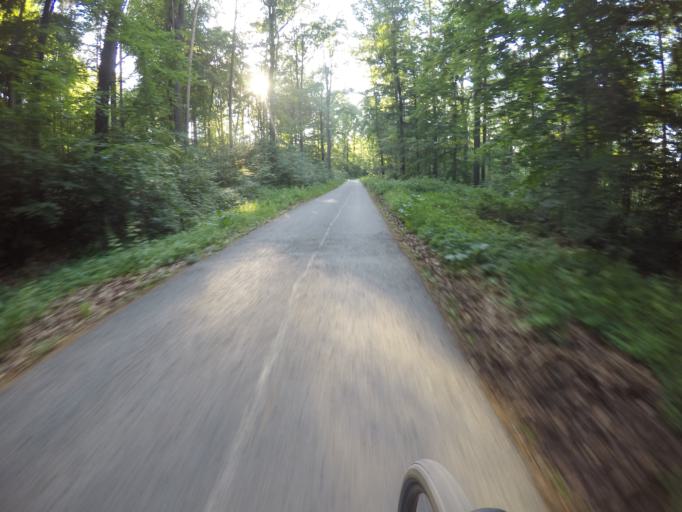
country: DE
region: Baden-Wuerttemberg
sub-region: Regierungsbezirk Stuttgart
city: Fellbach
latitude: 48.7855
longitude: 9.3010
